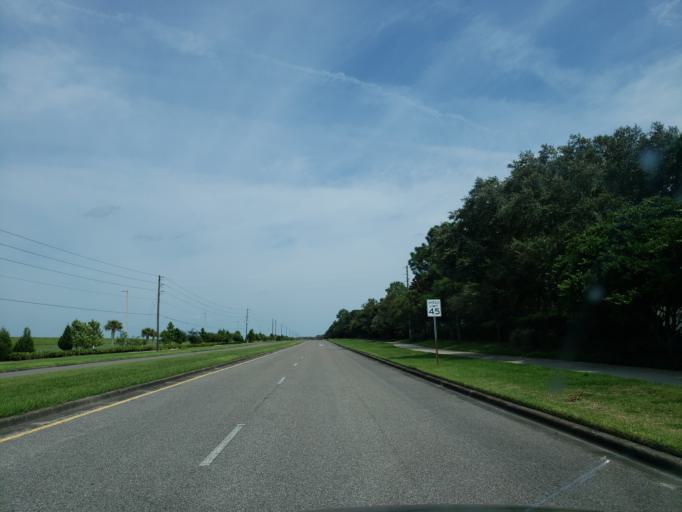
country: US
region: Florida
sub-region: Pasco County
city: Wesley Chapel
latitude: 28.2733
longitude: -82.3150
